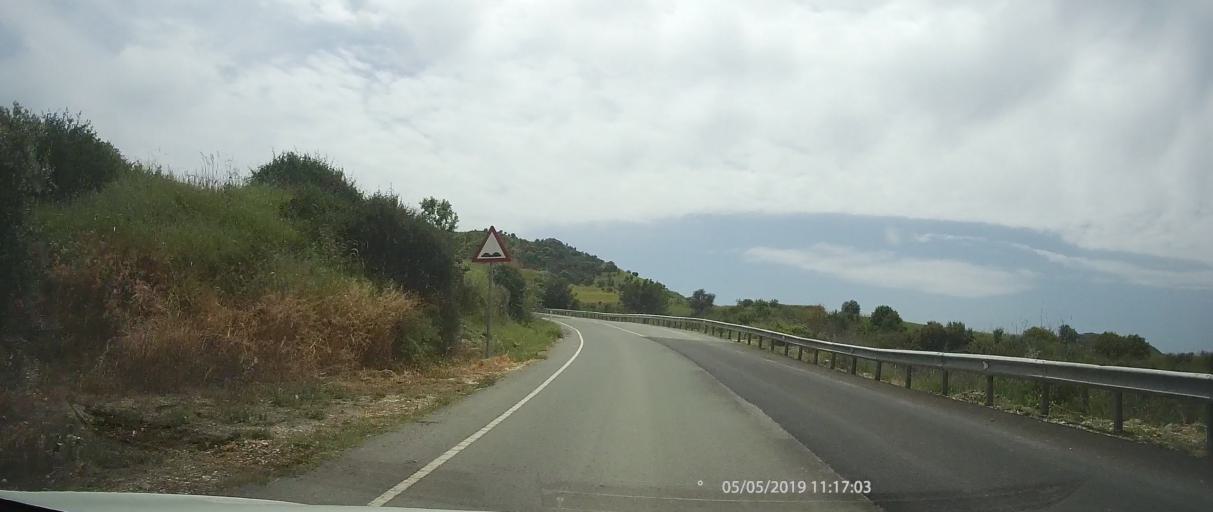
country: CY
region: Pafos
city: Mesogi
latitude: 34.9237
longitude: 32.5845
